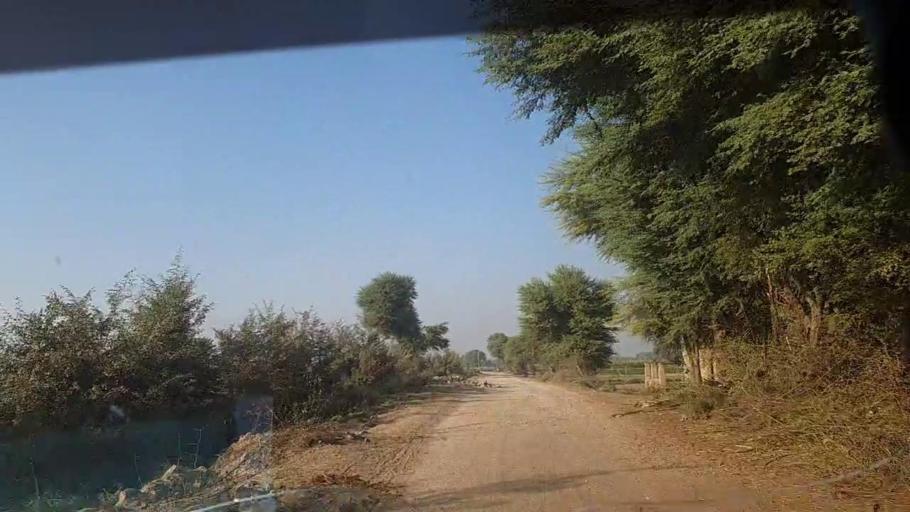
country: PK
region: Sindh
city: Sobhadero
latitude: 27.2611
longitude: 68.3505
